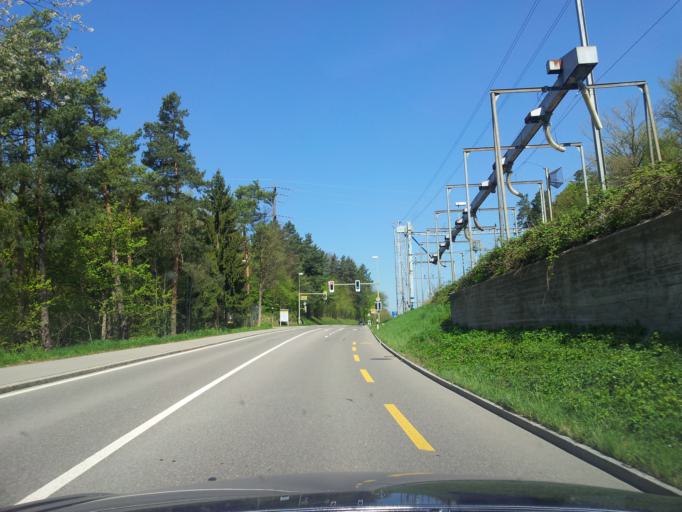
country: CH
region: Zurich
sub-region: Bezirk Dietikon
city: Birmensdorf
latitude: 47.3594
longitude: 8.4331
